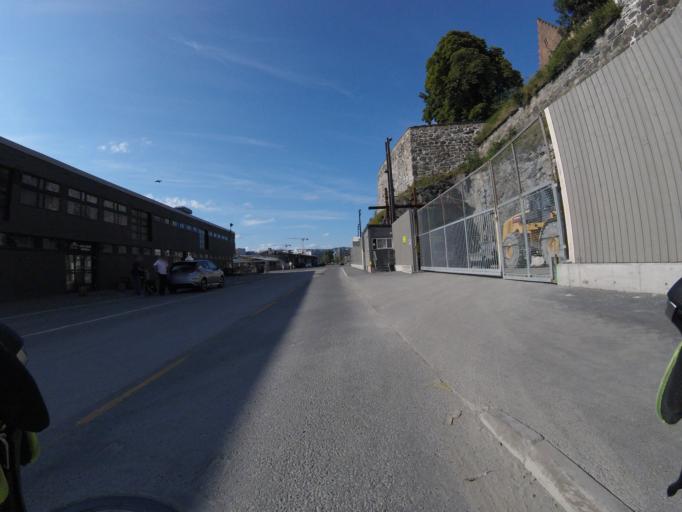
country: NO
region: Oslo
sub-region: Oslo
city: Oslo
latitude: 59.9066
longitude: 10.7353
